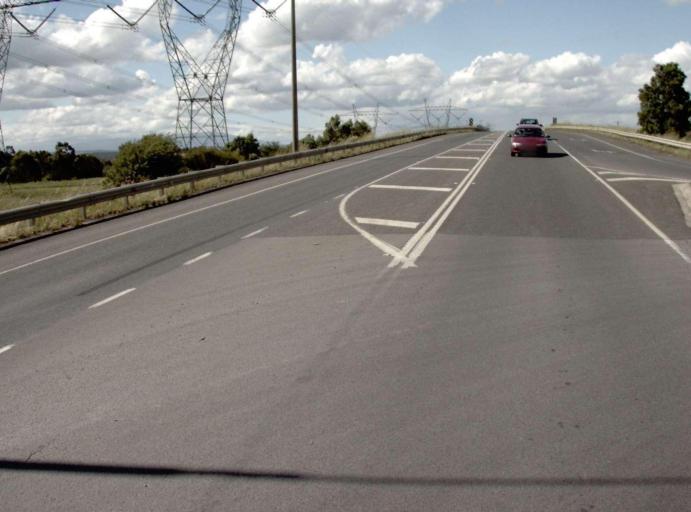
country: AU
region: Victoria
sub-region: Latrobe
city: Morwell
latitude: -38.2467
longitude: 146.4365
